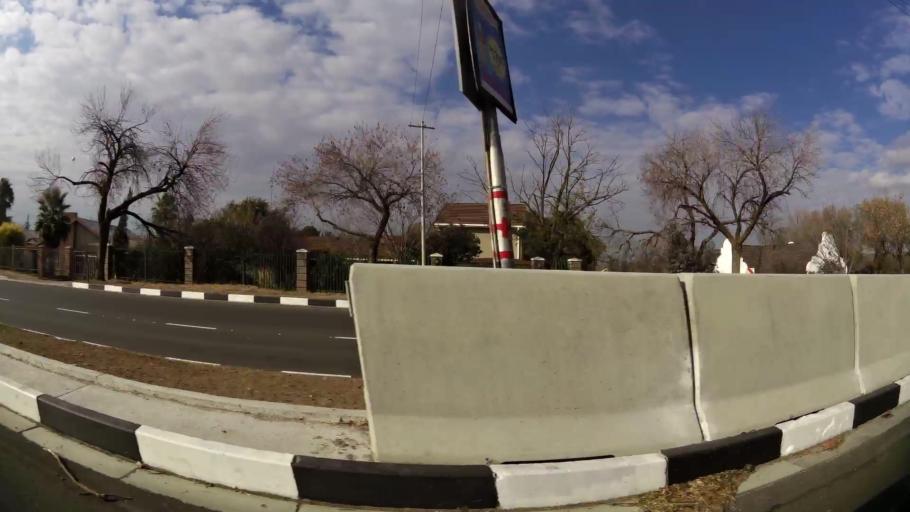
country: ZA
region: Orange Free State
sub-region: Mangaung Metropolitan Municipality
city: Bloemfontein
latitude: -29.0760
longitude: 26.2373
